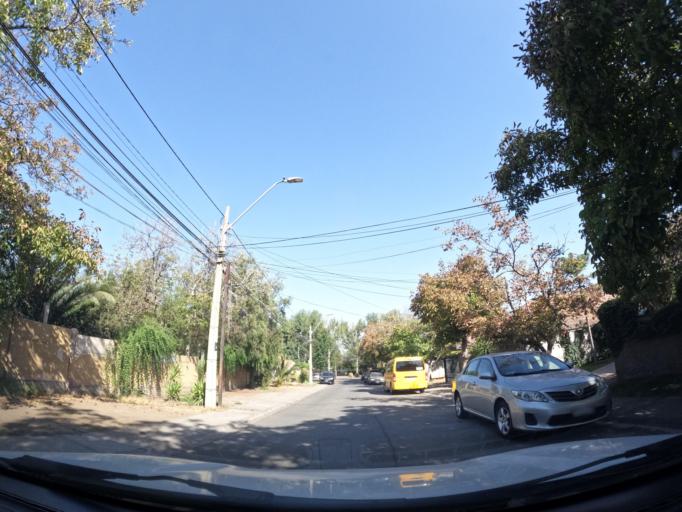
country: CL
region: Santiago Metropolitan
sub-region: Provincia de Santiago
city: Villa Presidente Frei, Nunoa, Santiago, Chile
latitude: -33.5055
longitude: -70.5595
